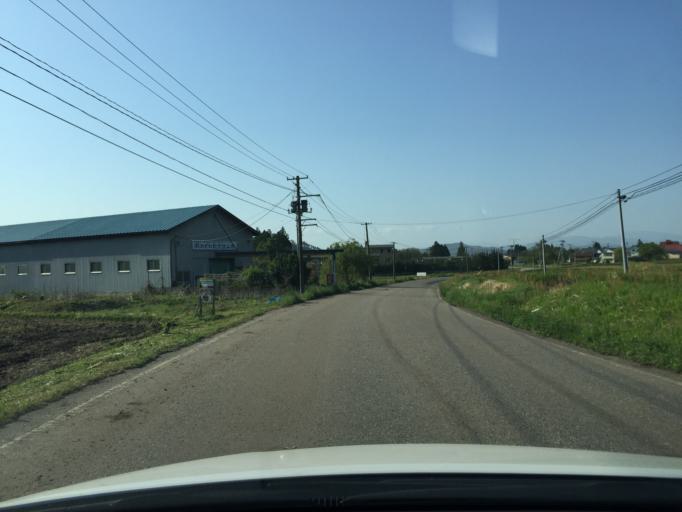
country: JP
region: Fukushima
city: Kitakata
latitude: 37.6576
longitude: 139.7745
